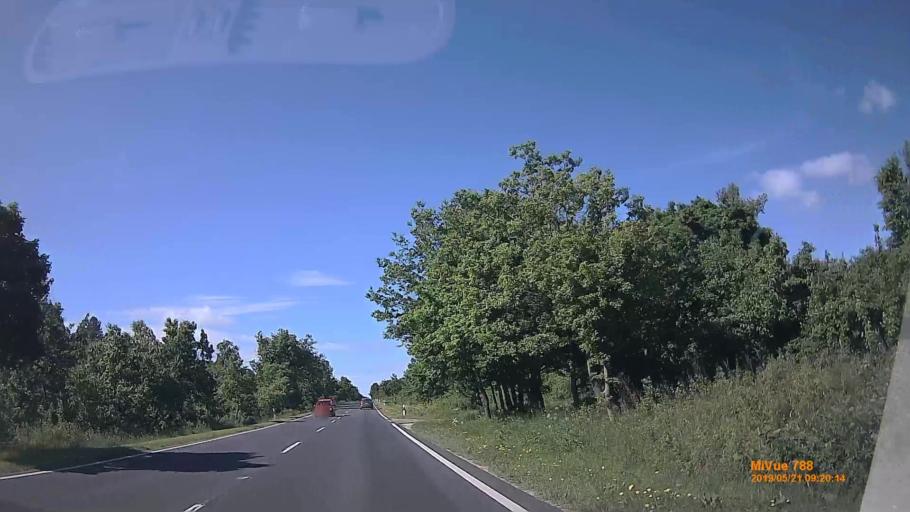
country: HU
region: Veszprem
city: Nemesvamos
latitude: 47.0322
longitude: 17.9129
